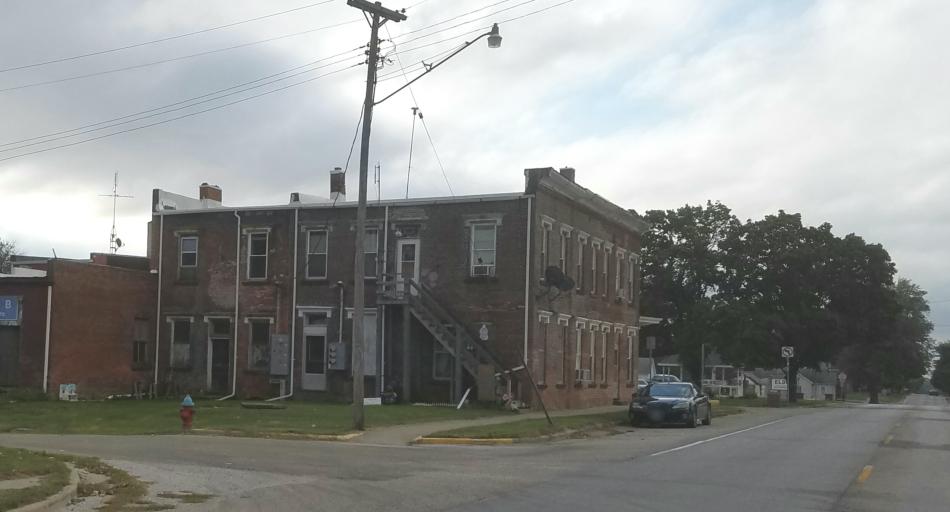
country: US
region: Illinois
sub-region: Fulton County
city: Astoria
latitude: 40.3665
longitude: -90.4252
